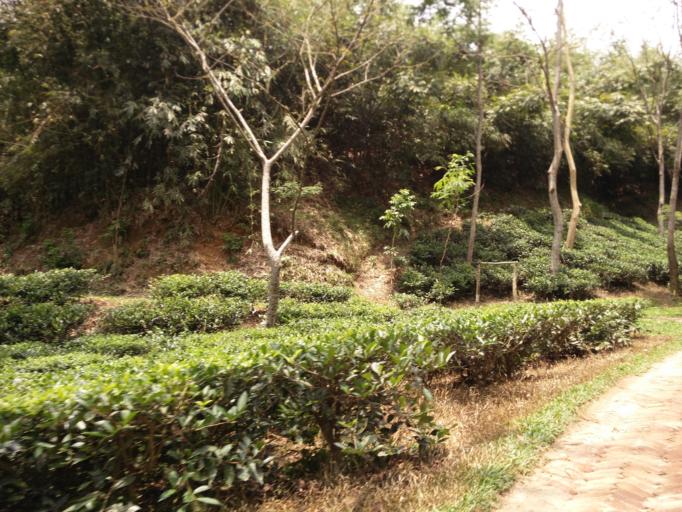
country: IN
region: Tripura
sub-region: Dhalai
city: Kamalpur
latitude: 24.3029
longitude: 91.7999
